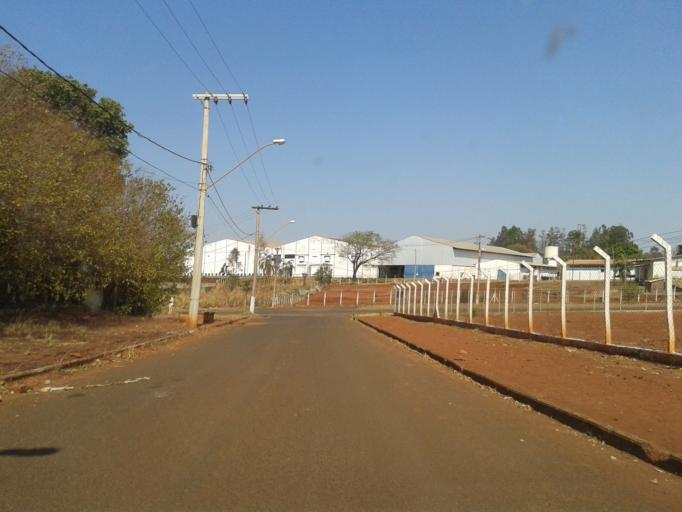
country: BR
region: Minas Gerais
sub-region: Ituiutaba
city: Ituiutaba
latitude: -18.9622
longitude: -49.4903
